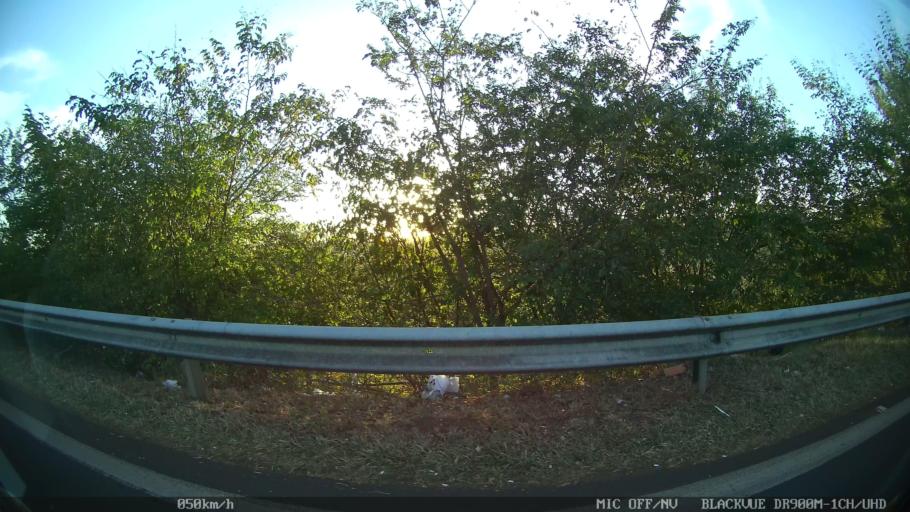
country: BR
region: Sao Paulo
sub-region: Franca
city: Franca
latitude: -20.5142
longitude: -47.4153
